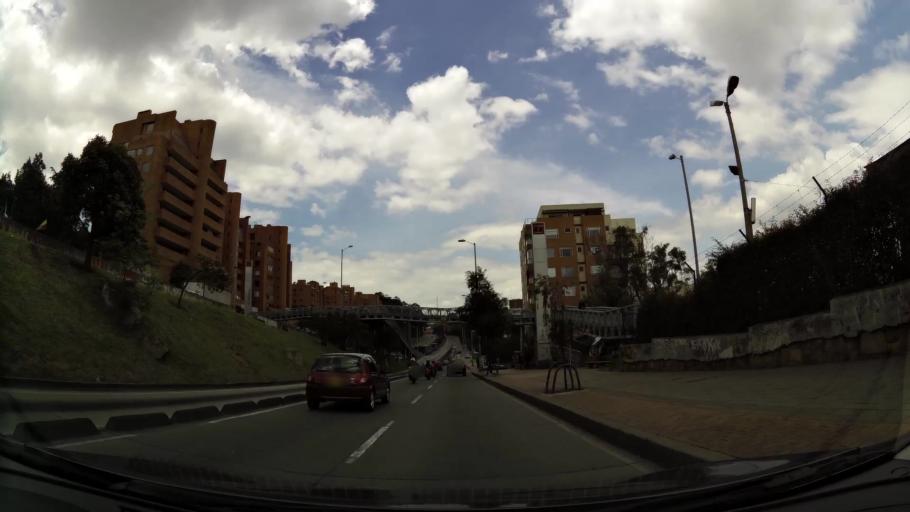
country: CO
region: Bogota D.C.
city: Barrio San Luis
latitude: 4.7256
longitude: -74.0747
